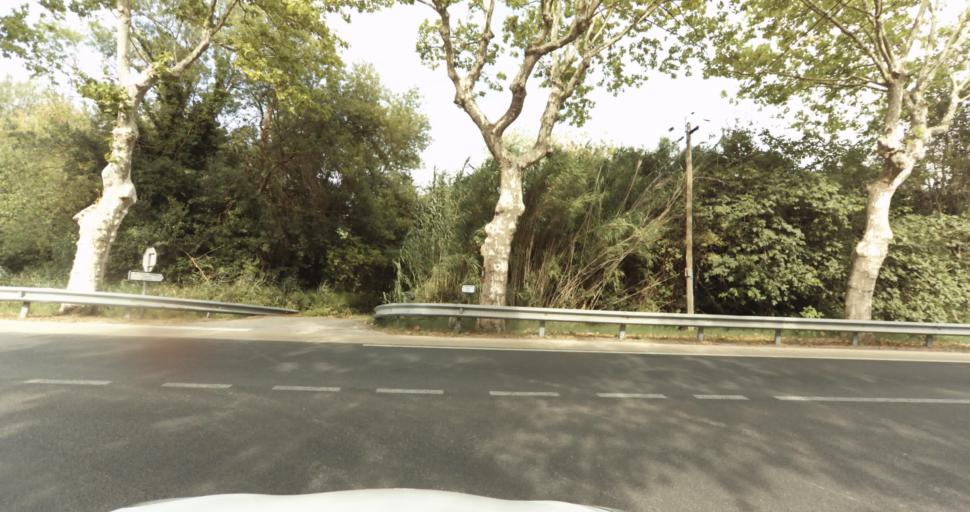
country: FR
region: Provence-Alpes-Cote d'Azur
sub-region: Departement des Bouches-du-Rhone
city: Saint-Chamas
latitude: 43.5677
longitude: 5.0242
